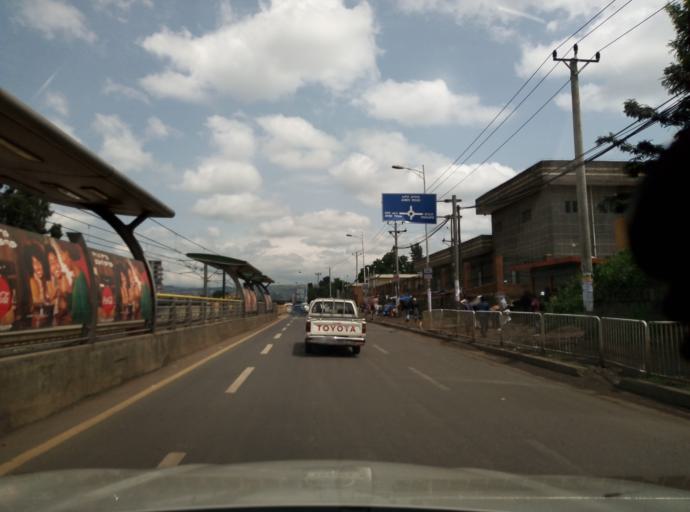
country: ET
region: Adis Abeba
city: Addis Ababa
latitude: 9.0114
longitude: 38.7231
